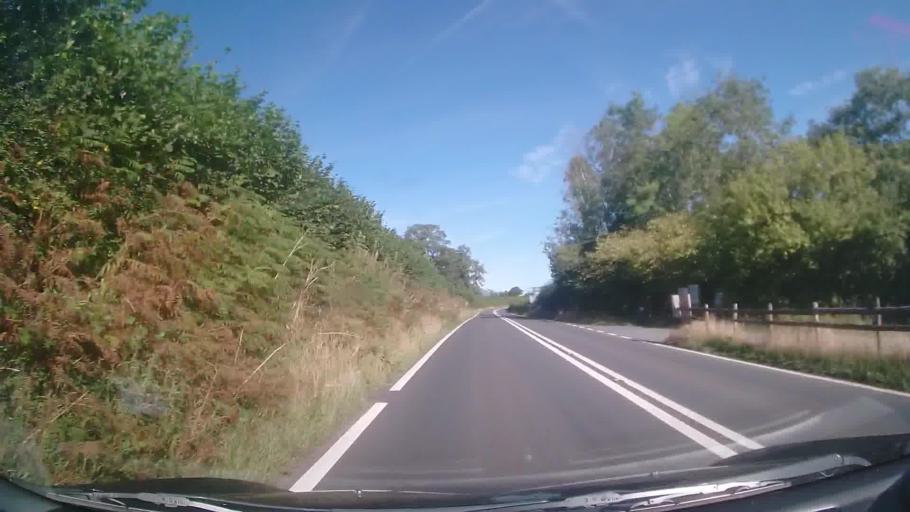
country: GB
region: Wales
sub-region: Sir Powys
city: Hay
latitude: 51.9595
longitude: -3.2041
